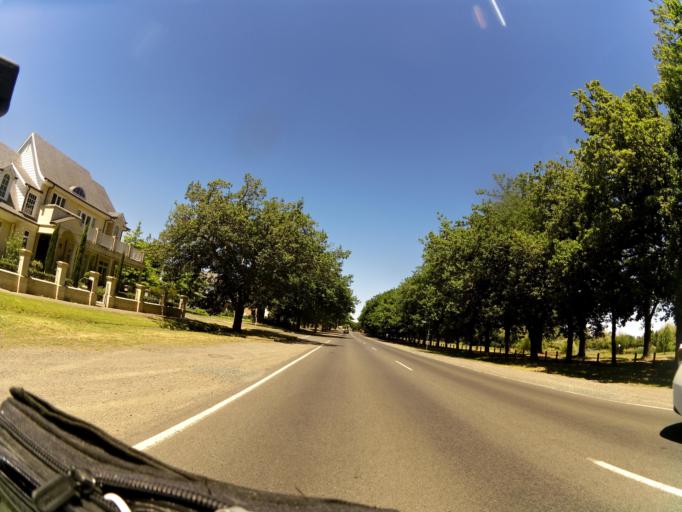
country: AU
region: Victoria
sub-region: Ballarat North
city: Newington
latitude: -37.5610
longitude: 143.8275
